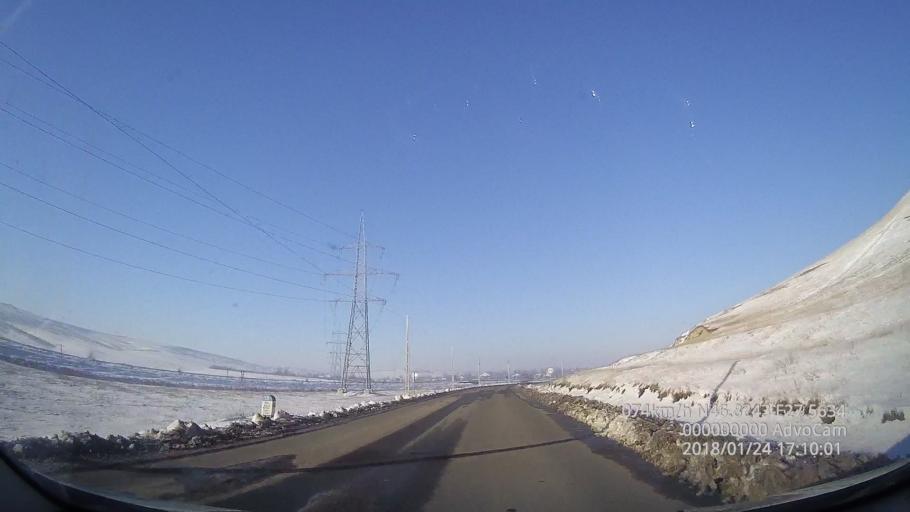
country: RO
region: Vaslui
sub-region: Comuna Vulturesti
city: Vulturesti
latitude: 46.8250
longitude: 27.5634
